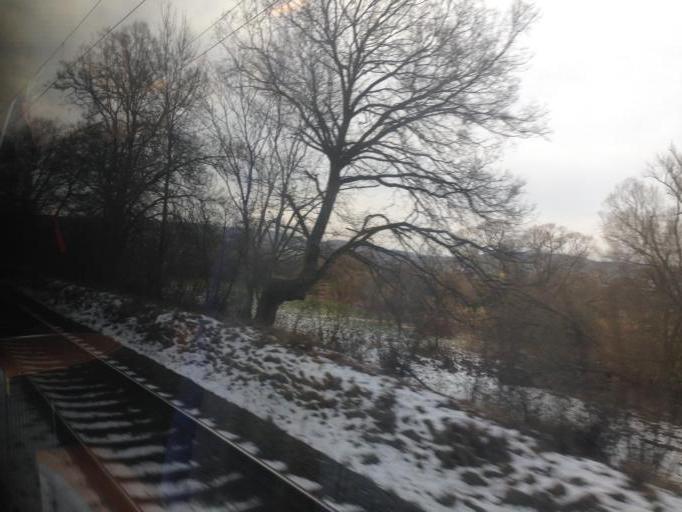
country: DE
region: Hesse
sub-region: Regierungsbezirk Giessen
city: Asslar
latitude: 50.5934
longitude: 8.4290
